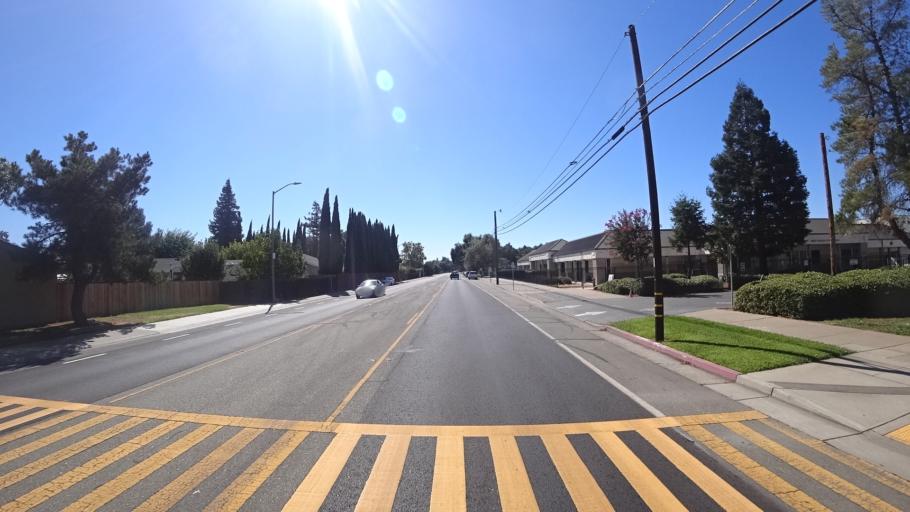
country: US
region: California
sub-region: Sacramento County
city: Elk Grove
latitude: 38.4003
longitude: -121.3715
